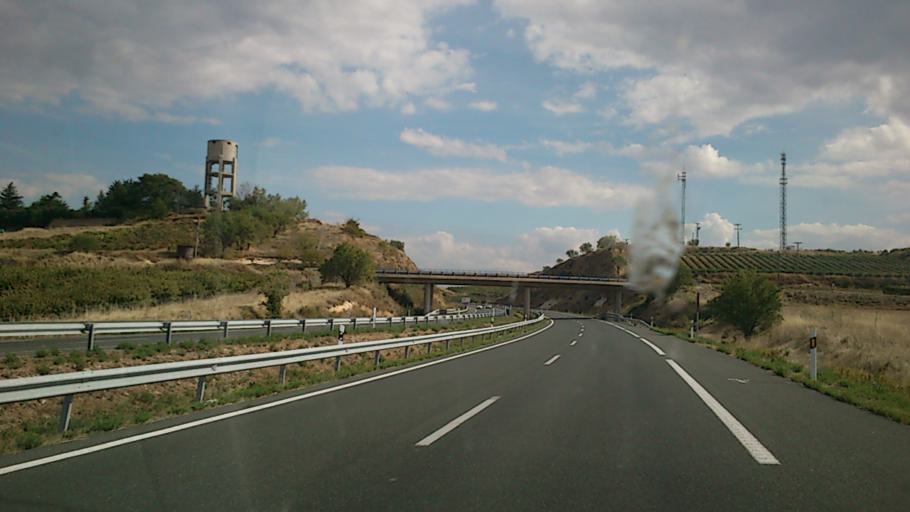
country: ES
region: La Rioja
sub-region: Provincia de La Rioja
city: Ollauri
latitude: 42.5401
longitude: -2.8403
